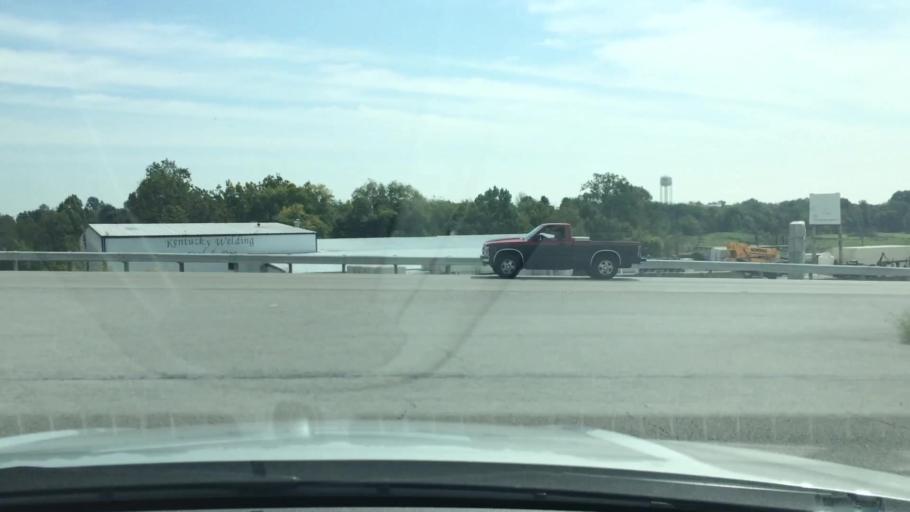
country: US
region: Kentucky
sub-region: Anderson County
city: Lawrenceburg
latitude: 38.0597
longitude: -84.9213
